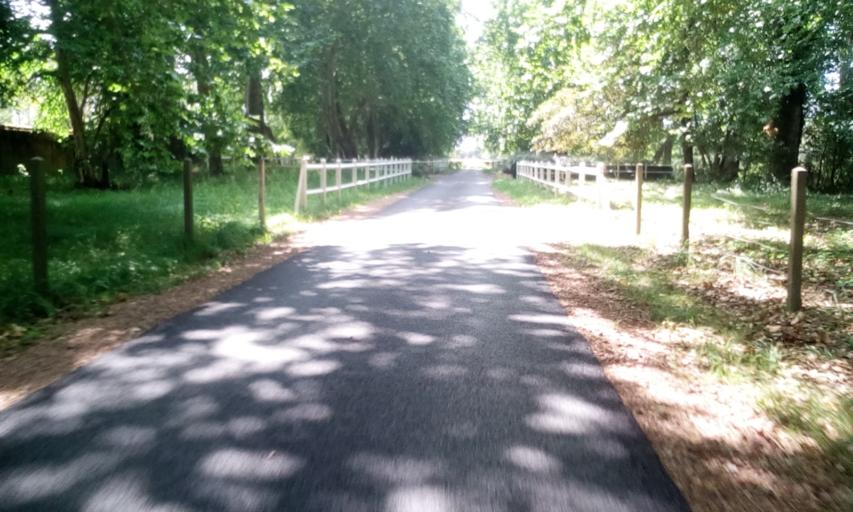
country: FR
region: Lower Normandy
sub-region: Departement du Calvados
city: Bellengreville
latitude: 49.1395
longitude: -0.2207
